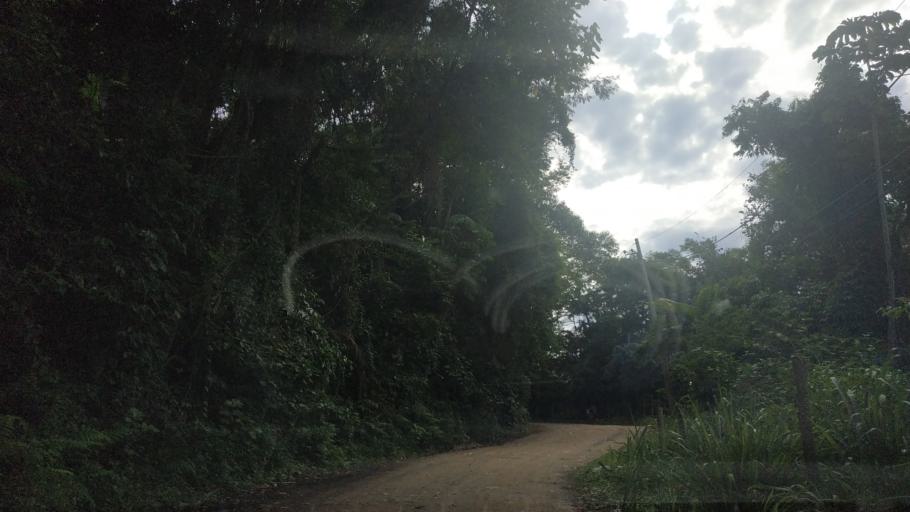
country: BR
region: Sao Paulo
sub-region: Ilhabela
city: Ilhabela
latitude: -23.8321
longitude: -45.3541
